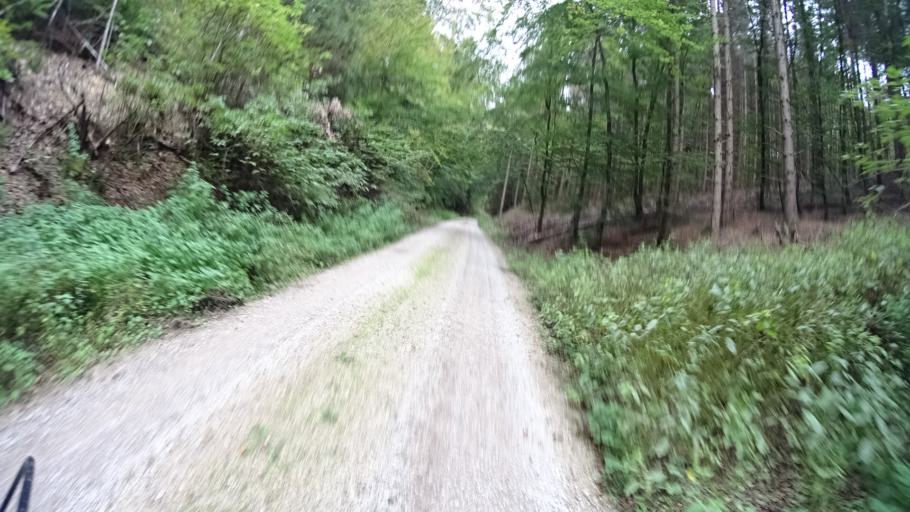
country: DE
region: Bavaria
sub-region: Upper Bavaria
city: Walting
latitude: 48.8980
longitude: 11.3053
